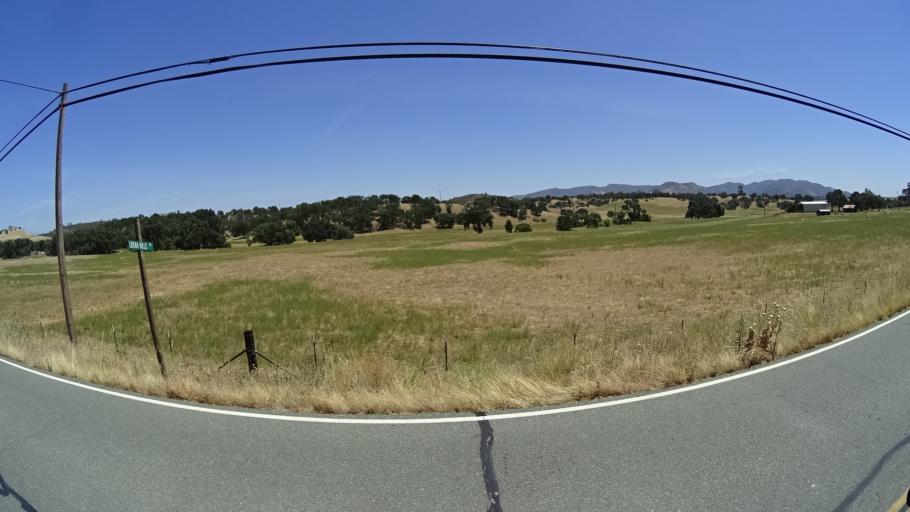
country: US
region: California
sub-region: Calaveras County
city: Valley Springs
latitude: 38.2039
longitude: -120.8276
